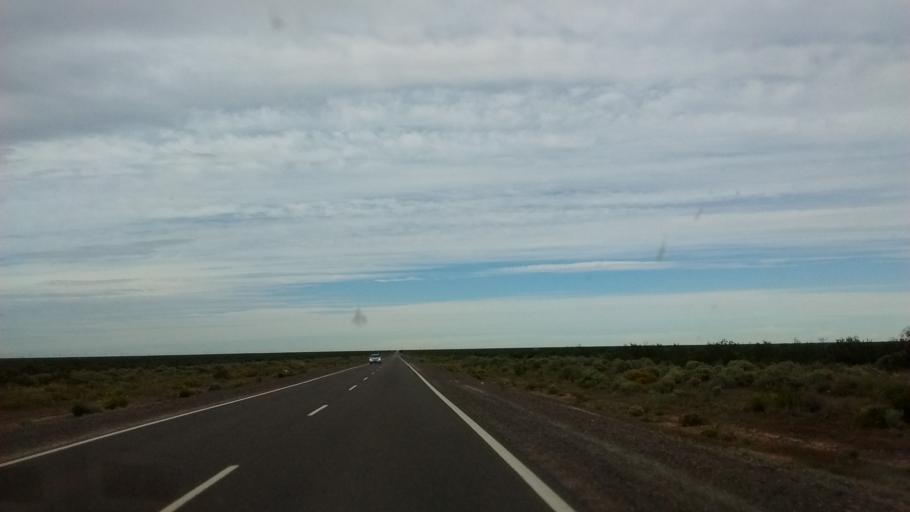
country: AR
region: Rio Negro
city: Contraalmirante Cordero
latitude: -38.4809
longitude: -68.0548
